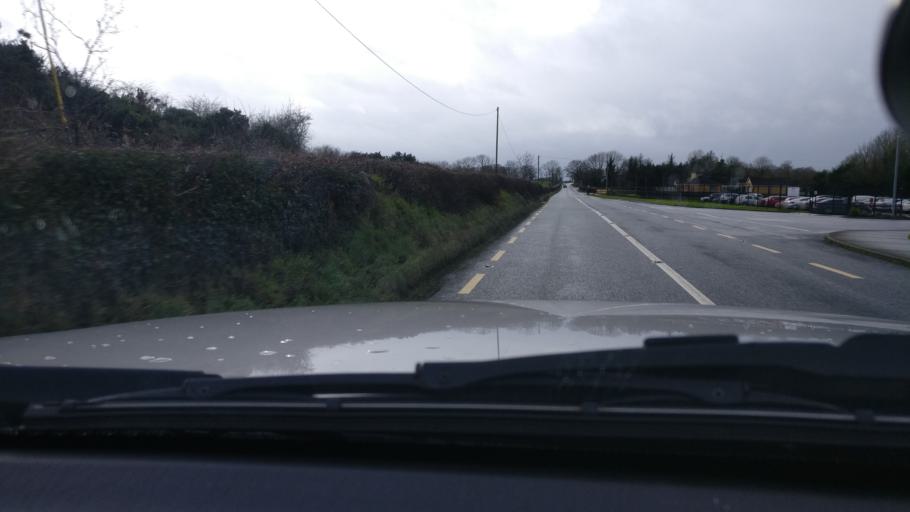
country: IE
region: Leinster
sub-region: An Longfort
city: Ballymahon
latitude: 53.5527
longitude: -7.7727
